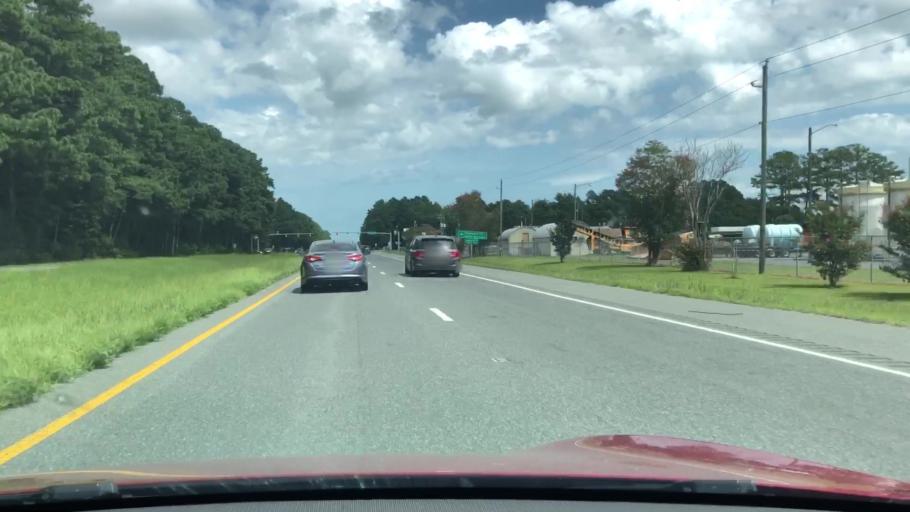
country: US
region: Virginia
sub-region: Accomack County
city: Accomac
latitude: 37.7252
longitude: -75.6758
